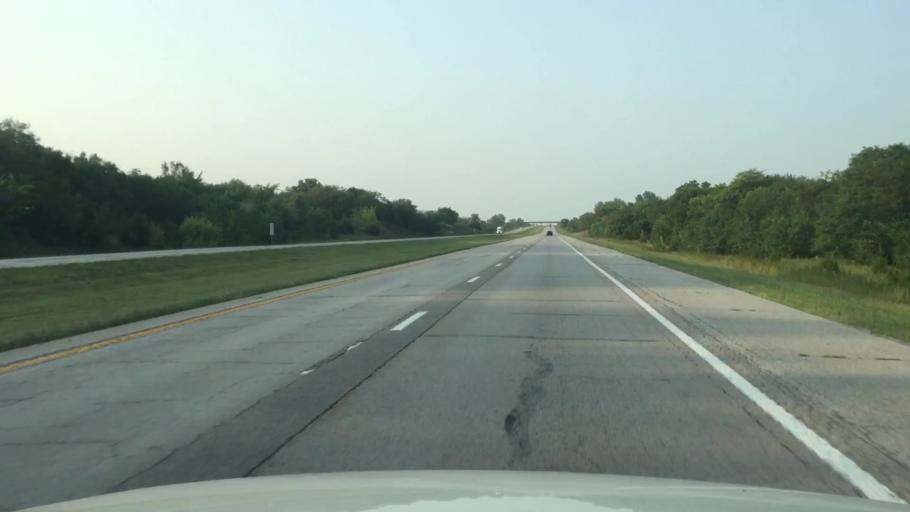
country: US
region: Missouri
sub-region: Harrison County
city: Bethany
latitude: 40.4047
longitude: -93.9943
